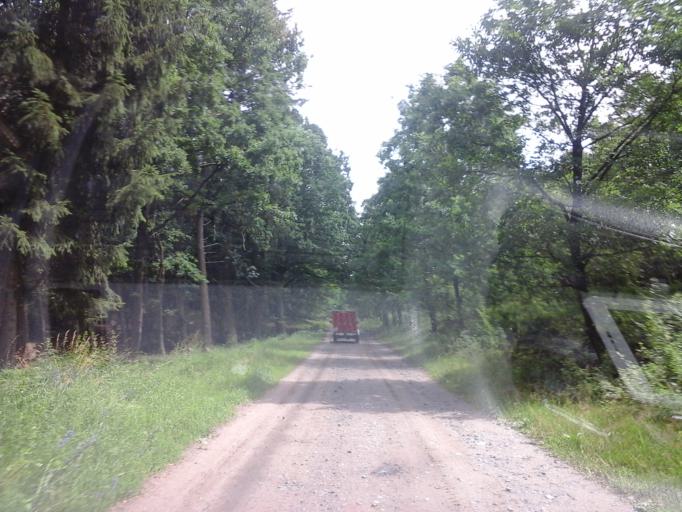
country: PL
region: West Pomeranian Voivodeship
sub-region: Powiat choszczenski
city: Bierzwnik
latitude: 52.9746
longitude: 15.6048
